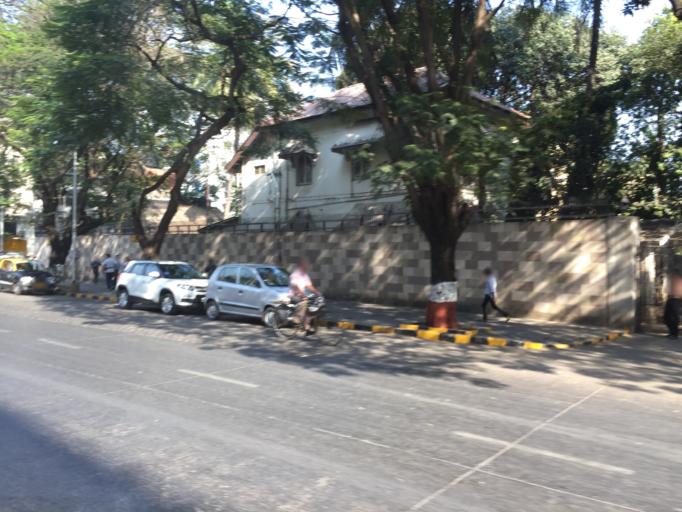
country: IN
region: Maharashtra
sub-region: Raigarh
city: Uran
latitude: 18.9339
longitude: 72.8369
